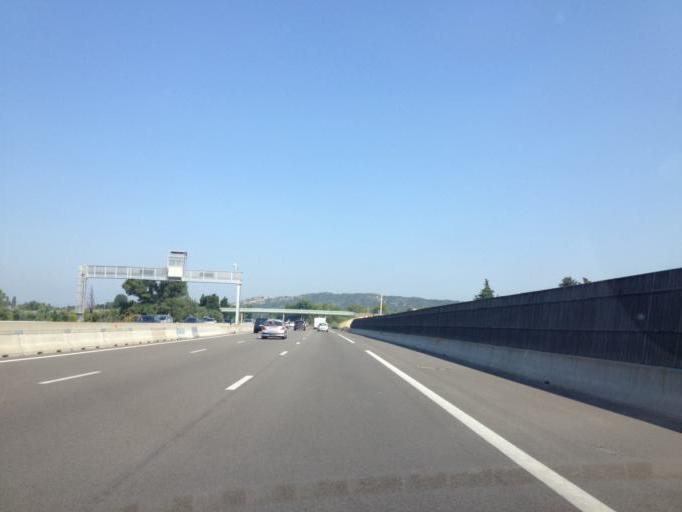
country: FR
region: Provence-Alpes-Cote d'Azur
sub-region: Departement du Vaucluse
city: Piolenc
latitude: 44.1823
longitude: 4.7524
